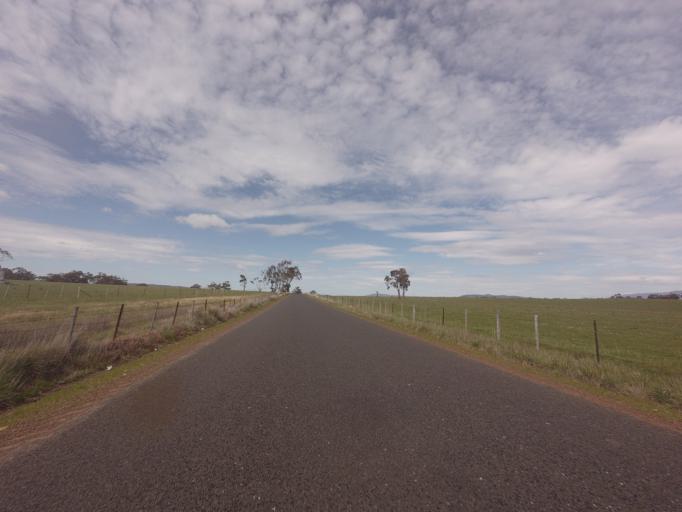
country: AU
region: Tasmania
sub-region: Northern Midlands
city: Evandale
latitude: -41.7879
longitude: 147.2439
